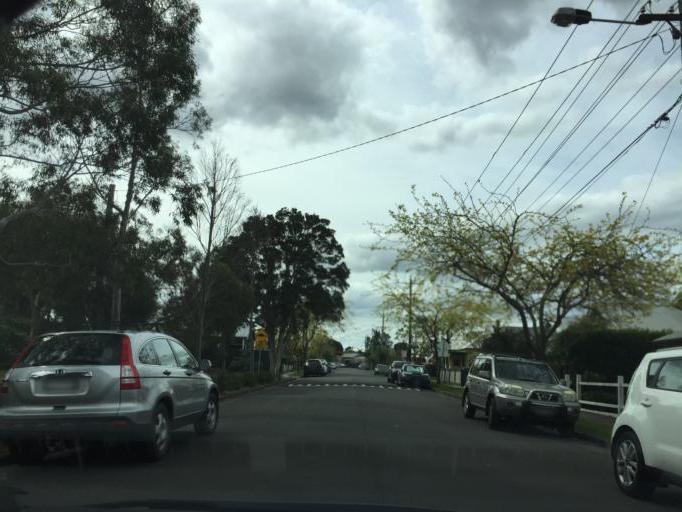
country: AU
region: Victoria
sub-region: Maribyrnong
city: Kingsville
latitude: -37.8075
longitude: 144.8803
